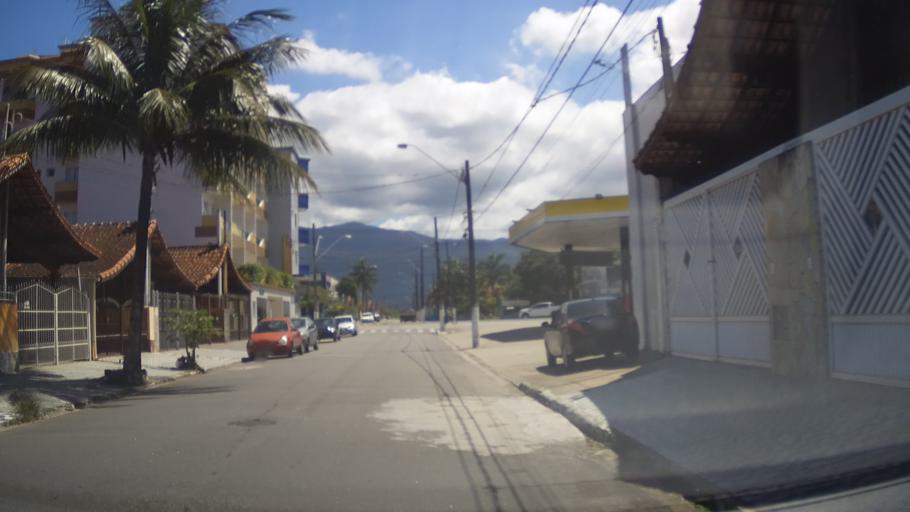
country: BR
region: Sao Paulo
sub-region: Mongagua
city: Mongagua
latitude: -24.0437
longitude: -46.5209
